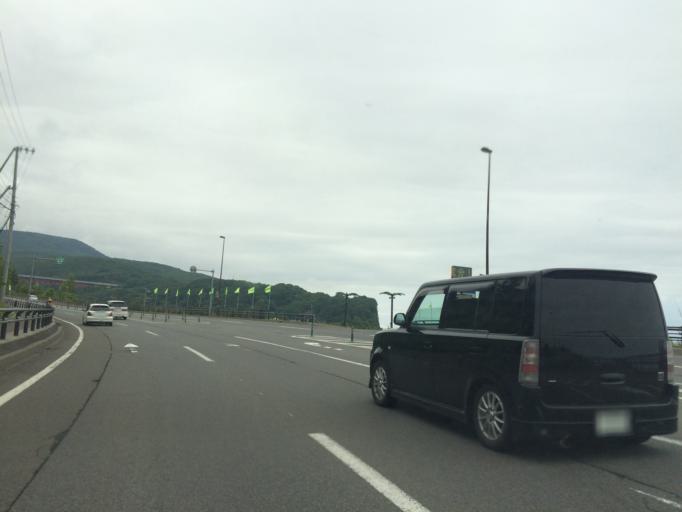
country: JP
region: Hokkaido
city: Otaru
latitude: 43.1531
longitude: 141.1279
